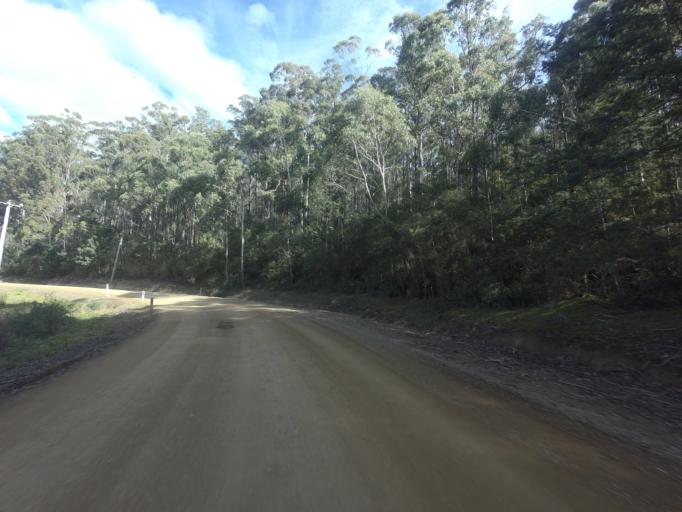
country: AU
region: Tasmania
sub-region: Clarence
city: Sandford
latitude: -43.1269
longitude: 147.7624
